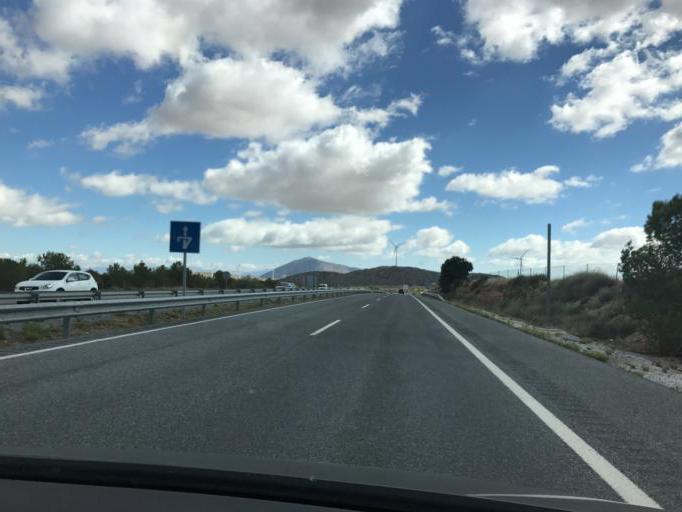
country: ES
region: Andalusia
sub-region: Provincia de Granada
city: Zujar
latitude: 37.4799
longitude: -2.8535
